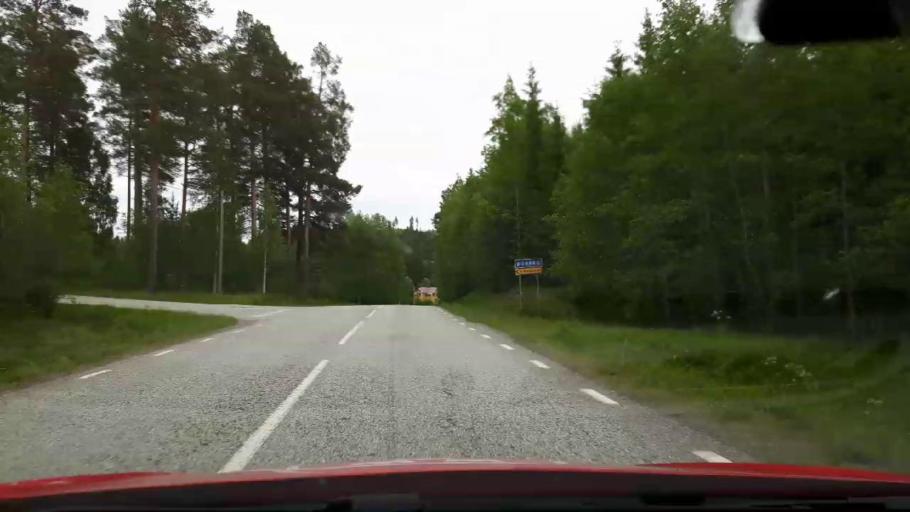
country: SE
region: Jaemtland
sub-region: Stroemsunds Kommun
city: Stroemsund
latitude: 63.3403
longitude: 15.7605
